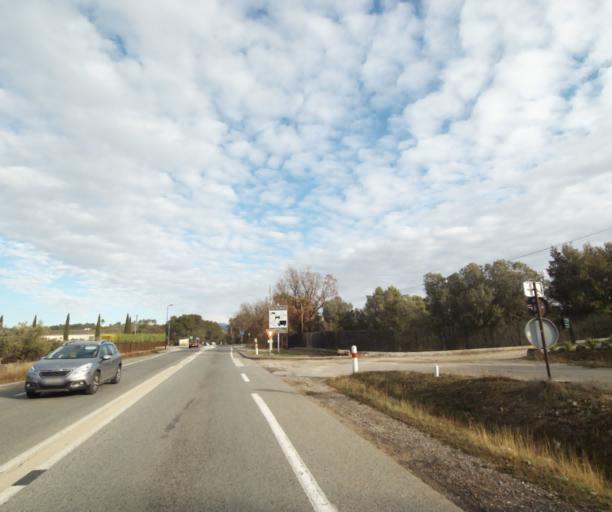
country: FR
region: Provence-Alpes-Cote d'Azur
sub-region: Departement du Var
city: Trans-en-Provence
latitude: 43.4880
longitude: 6.4833
